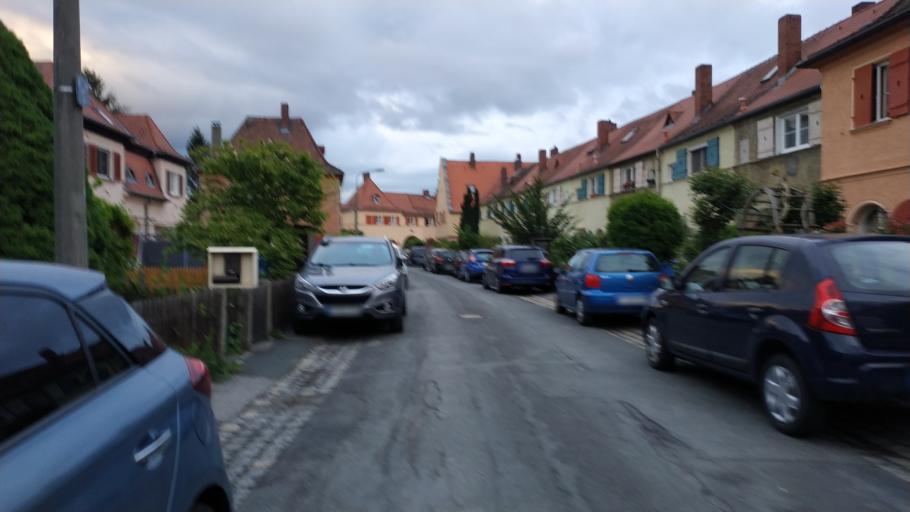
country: DE
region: Bavaria
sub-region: Regierungsbezirk Mittelfranken
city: Nuernberg
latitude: 49.4234
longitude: 11.0591
